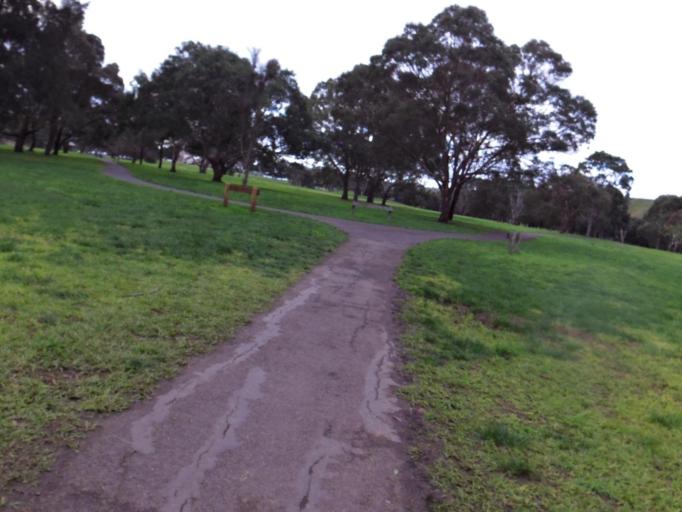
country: AU
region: Victoria
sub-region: Greater Geelong
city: Wandana Heights
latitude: -38.1456
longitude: 144.3095
